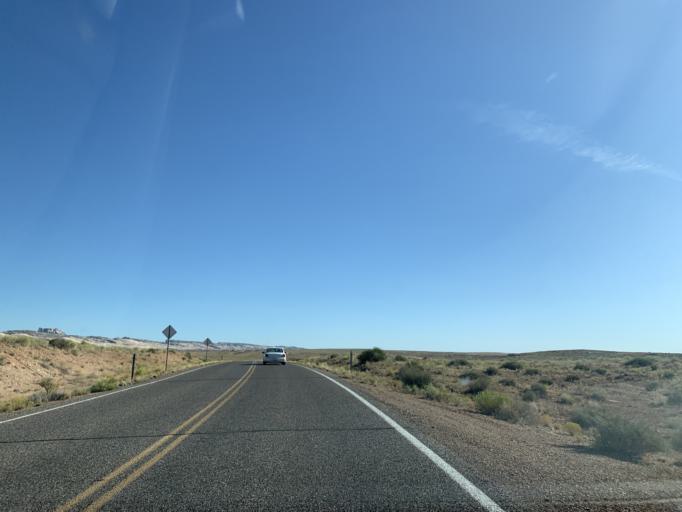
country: US
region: Utah
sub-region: Emery County
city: Ferron
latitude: 38.5720
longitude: -110.7083
